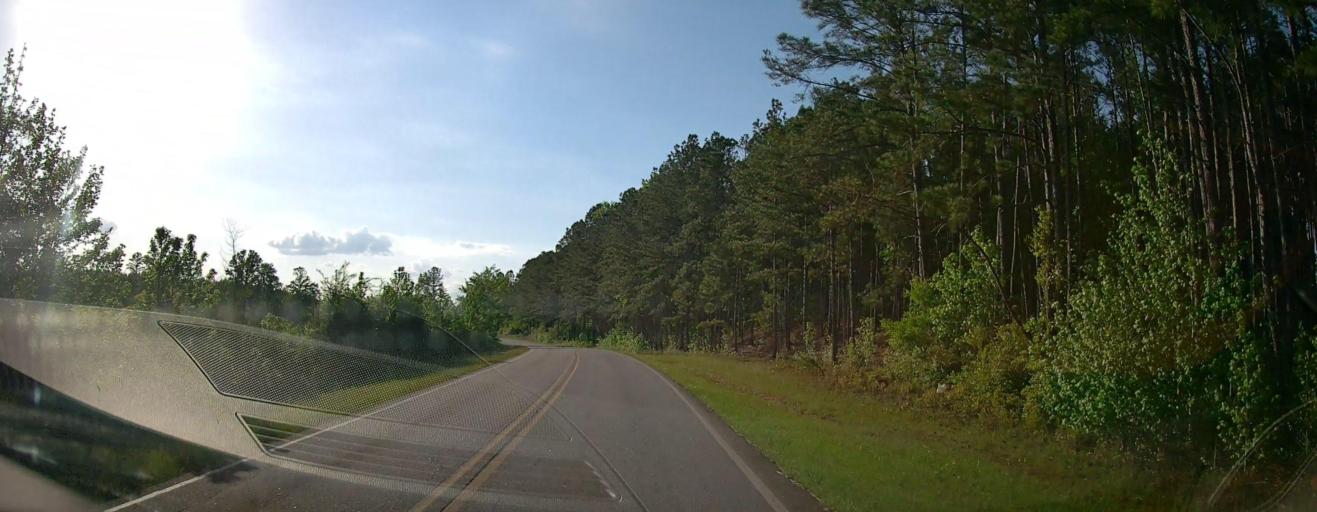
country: US
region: Georgia
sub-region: Putnam County
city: Eatonton
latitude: 33.2817
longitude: -83.3163
